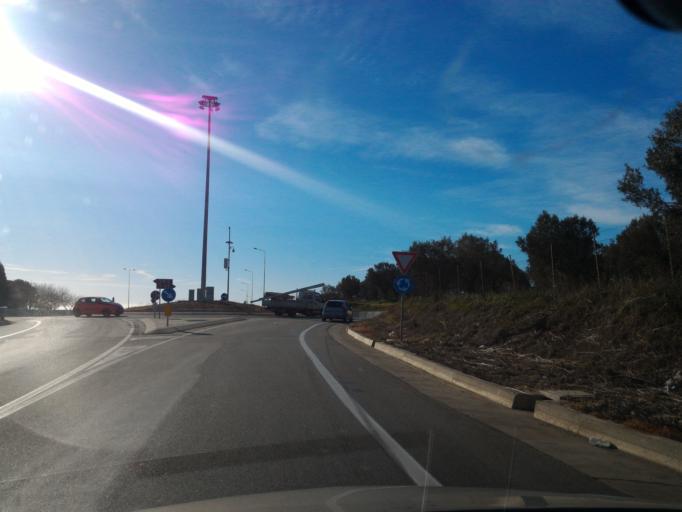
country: IT
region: Calabria
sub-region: Provincia di Crotone
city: Isola di Capo Rizzuto
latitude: 38.9511
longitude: 17.0826
